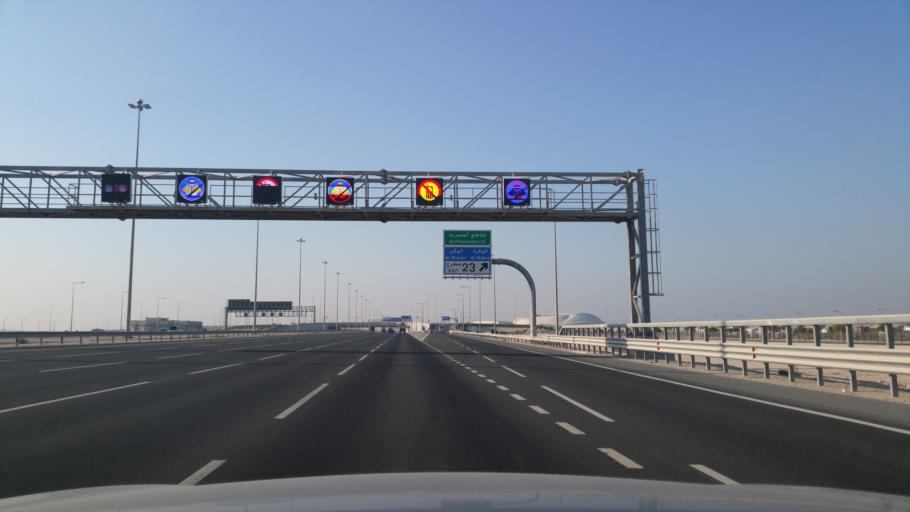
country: QA
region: Al Wakrah
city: Al Wakrah
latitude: 25.1433
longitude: 51.5795
